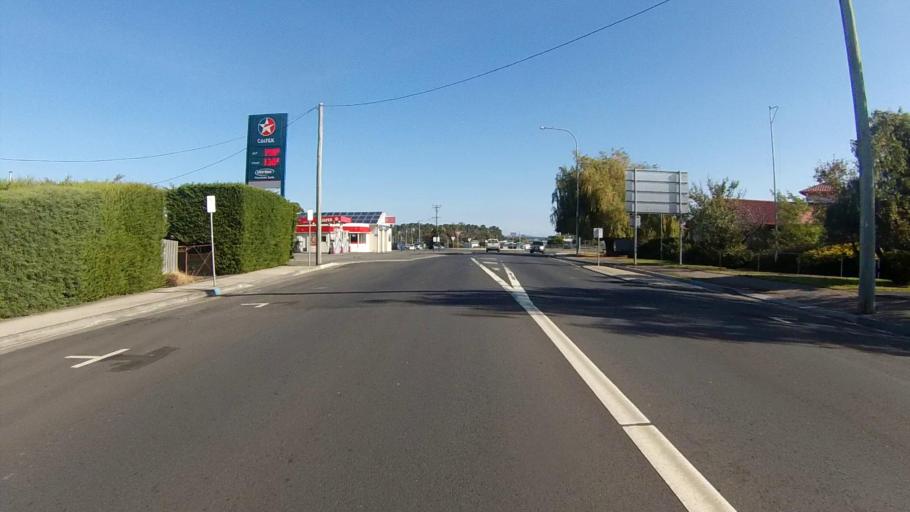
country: AU
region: Tasmania
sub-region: Sorell
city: Sorell
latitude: -42.7853
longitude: 147.5618
